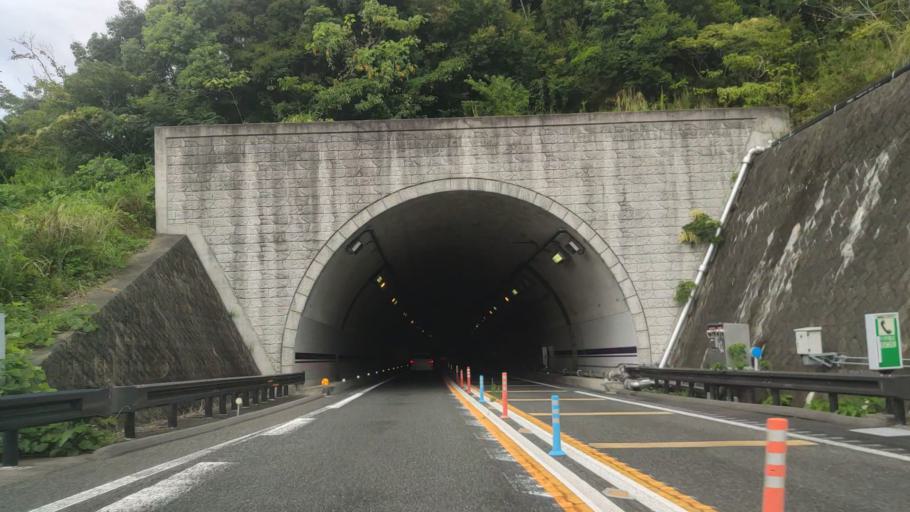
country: JP
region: Wakayama
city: Tanabe
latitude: 33.7467
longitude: 135.3683
